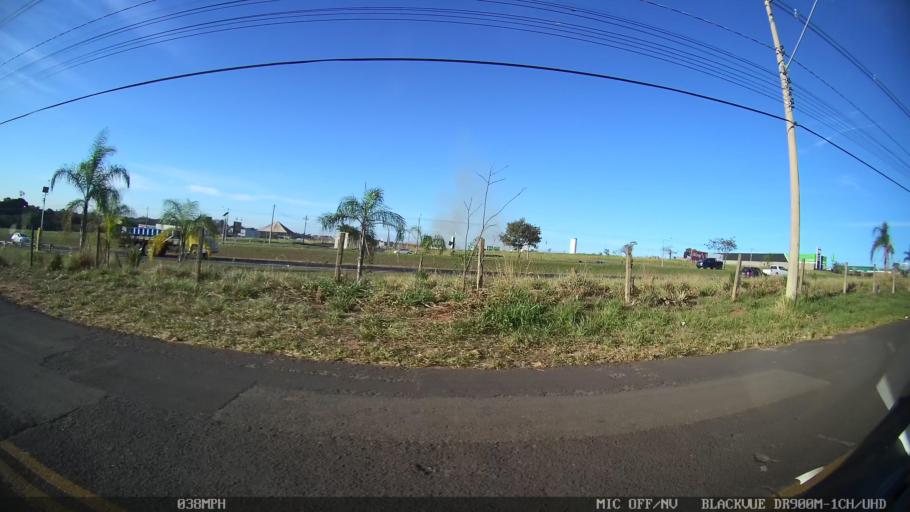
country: BR
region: Sao Paulo
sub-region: Sao Jose Do Rio Preto
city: Sao Jose do Rio Preto
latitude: -20.8624
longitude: -49.3340
